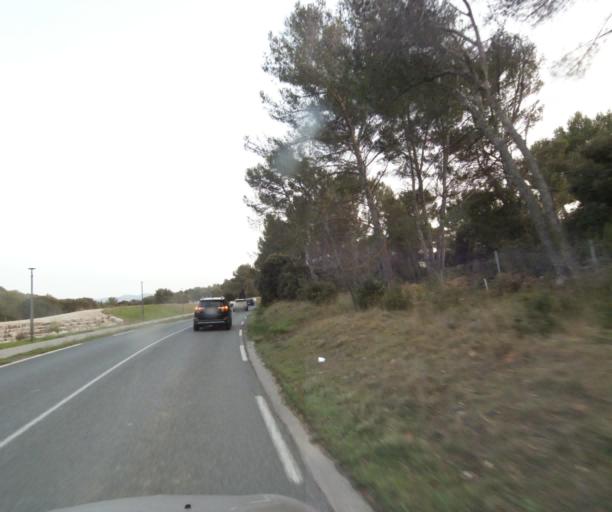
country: FR
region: Provence-Alpes-Cote d'Azur
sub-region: Departement des Bouches-du-Rhone
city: Cabries
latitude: 43.4551
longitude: 5.3561
